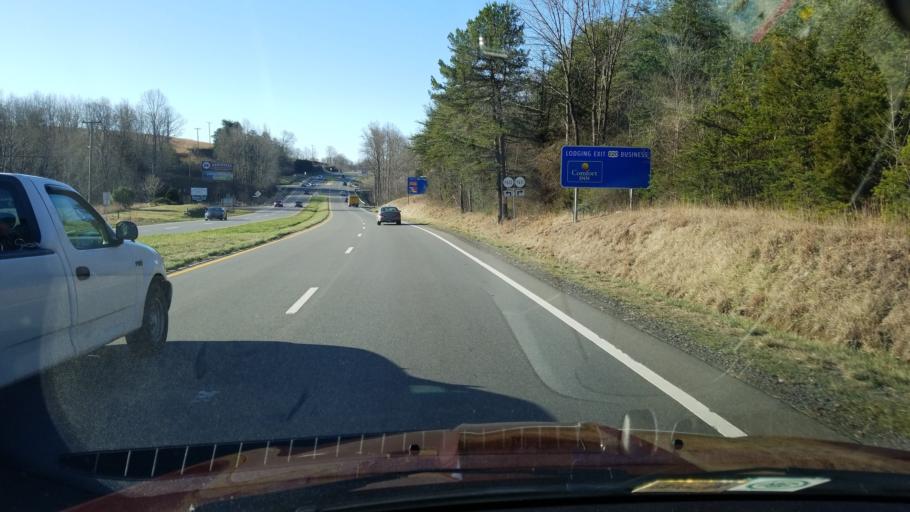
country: US
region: Virginia
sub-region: Franklin County
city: Rocky Mount
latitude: 37.0313
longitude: -79.8793
